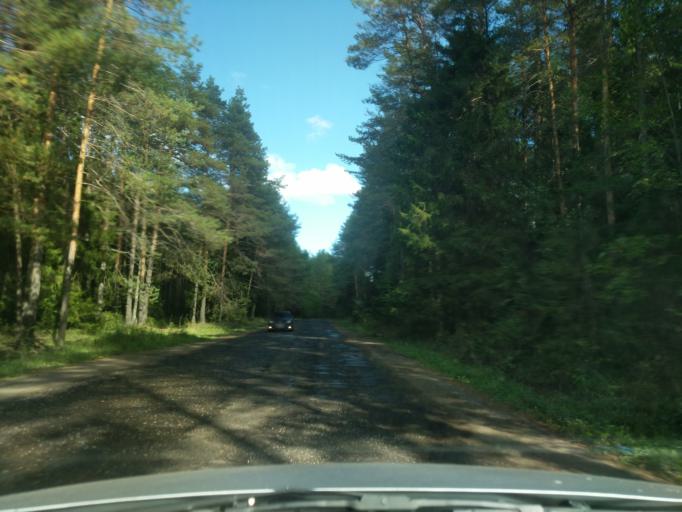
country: RU
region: Kirov
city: Kirovo-Chepetsk
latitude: 58.6053
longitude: 49.9178
